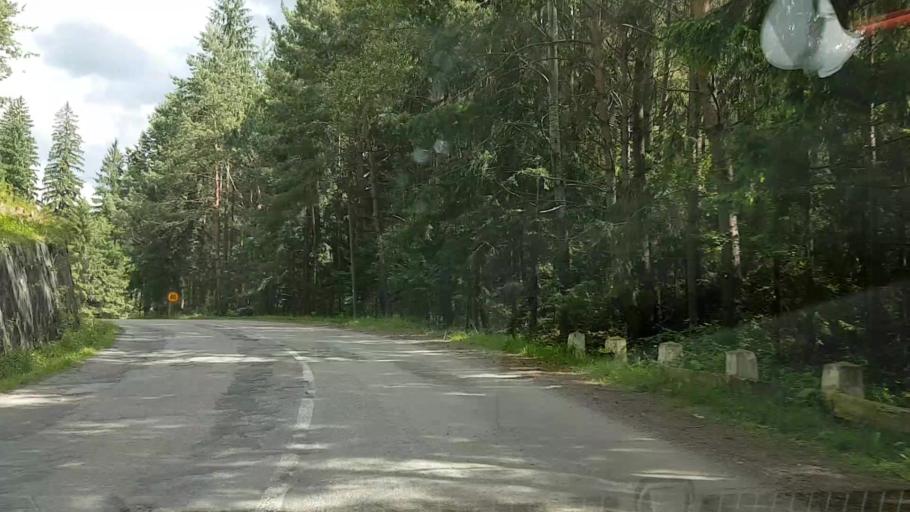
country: RO
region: Neamt
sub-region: Comuna Hangu
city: Hangu
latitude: 47.0510
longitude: 26.0065
